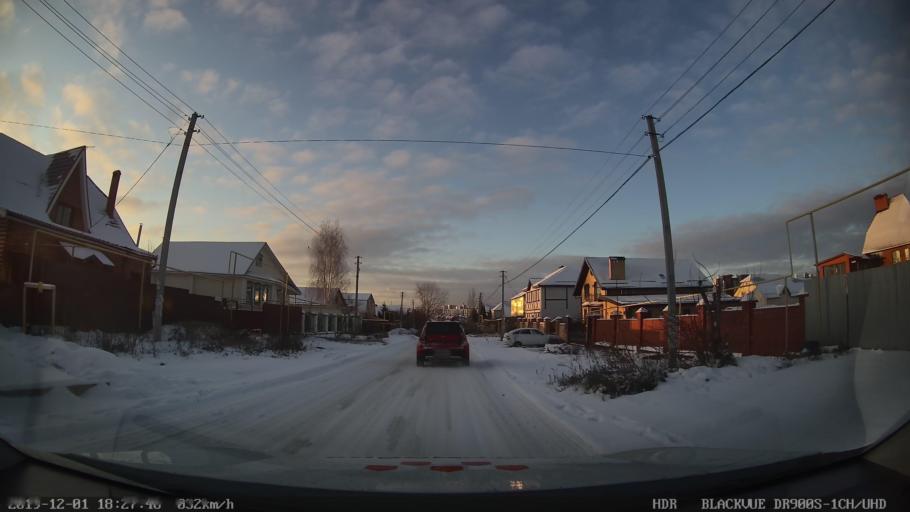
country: RU
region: Tatarstan
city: Vysokaya Gora
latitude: 55.8033
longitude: 49.2519
